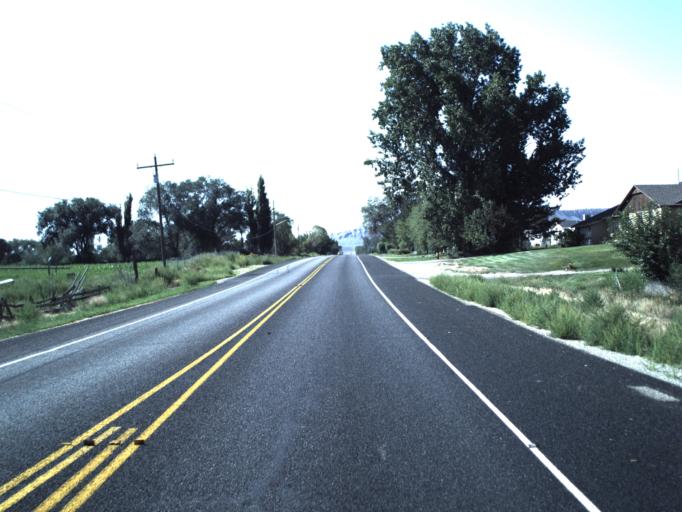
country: US
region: Utah
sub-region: Emery County
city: Ferron
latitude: 39.0798
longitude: -111.1318
